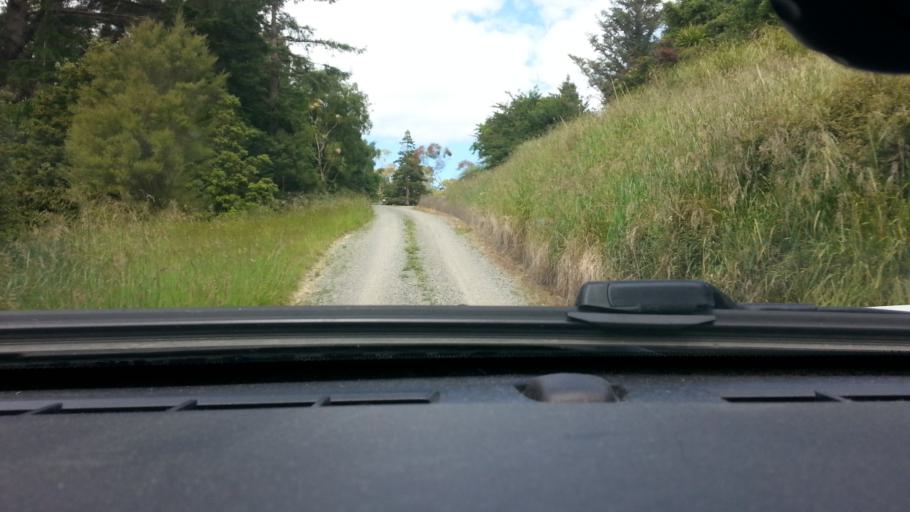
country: NZ
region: Wellington
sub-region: South Wairarapa District
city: Waipawa
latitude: -41.1990
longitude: 175.6060
